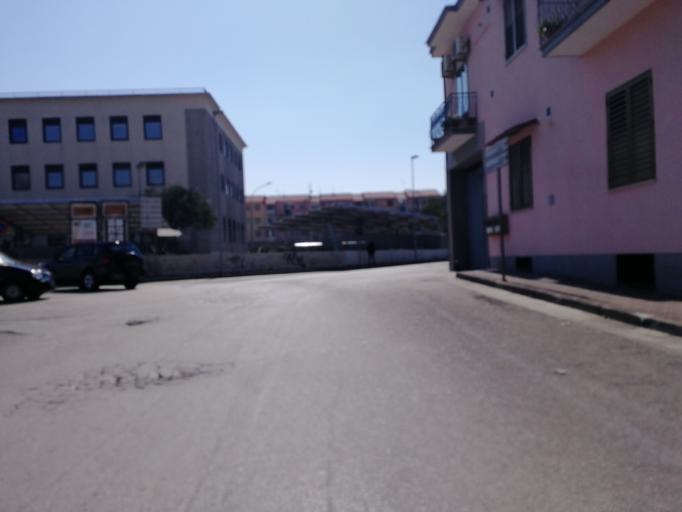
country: IT
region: Campania
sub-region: Provincia di Caserta
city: Santa Maria Capua Vetere
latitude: 41.0879
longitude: 14.2559
